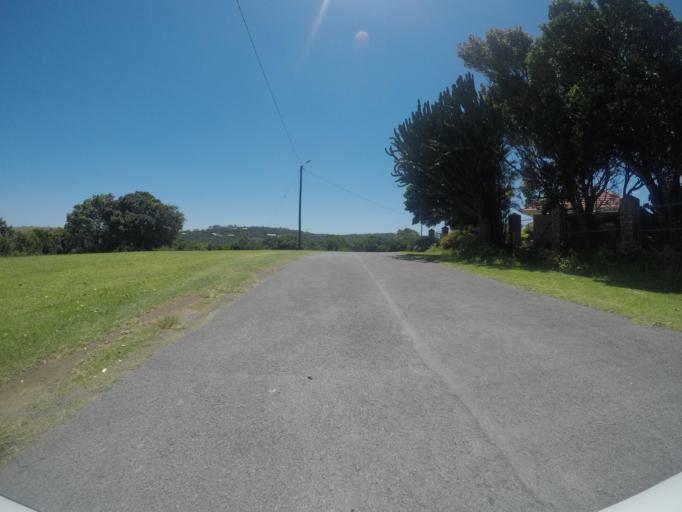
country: ZA
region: Eastern Cape
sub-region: Buffalo City Metropolitan Municipality
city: East London
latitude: -32.9373
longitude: 28.0236
